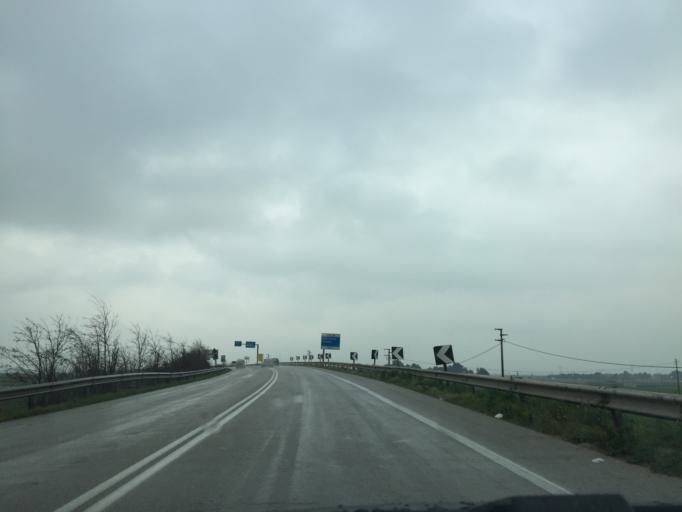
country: IT
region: Apulia
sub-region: Provincia di Foggia
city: Foggia
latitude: 41.4768
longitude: 15.5109
